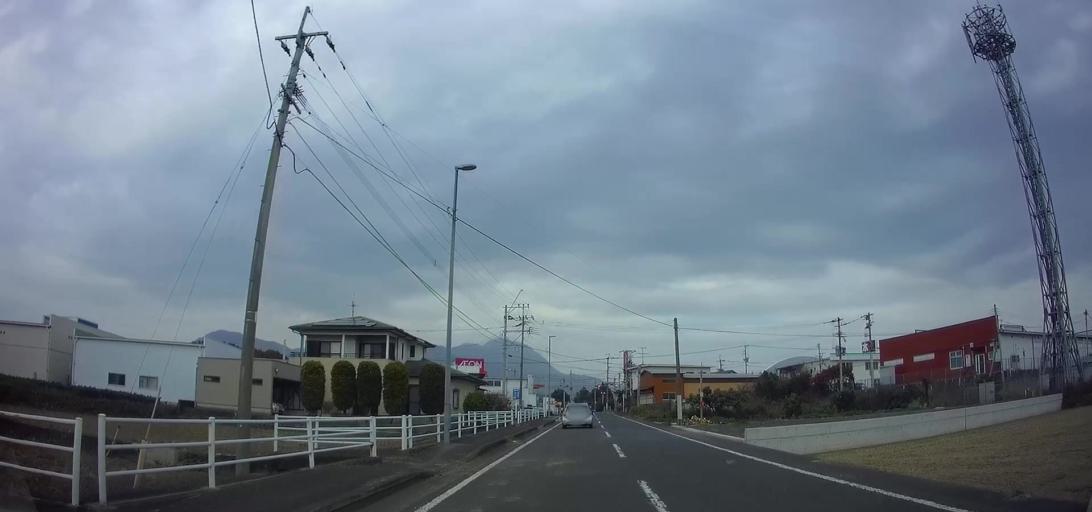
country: JP
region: Nagasaki
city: Shimabara
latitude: 32.6614
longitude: 130.3106
